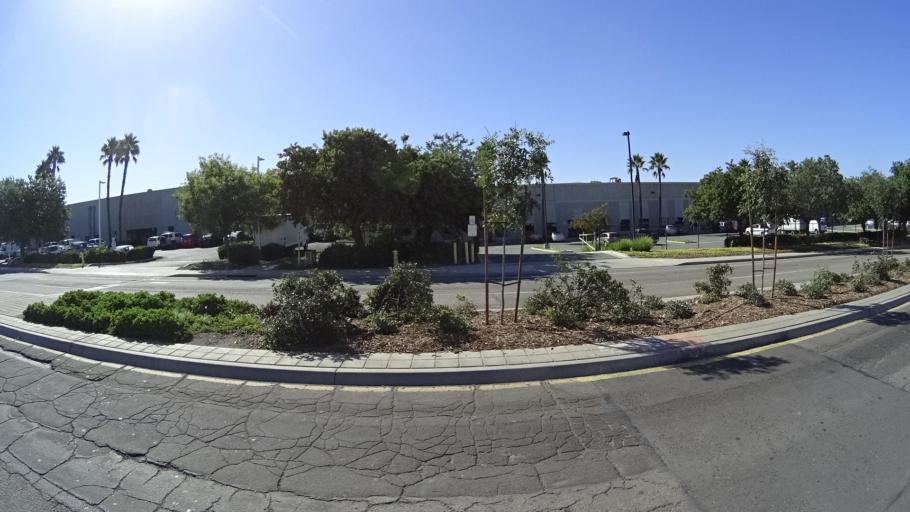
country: MX
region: Baja California
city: Tijuana
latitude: 32.5603
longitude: -116.9371
